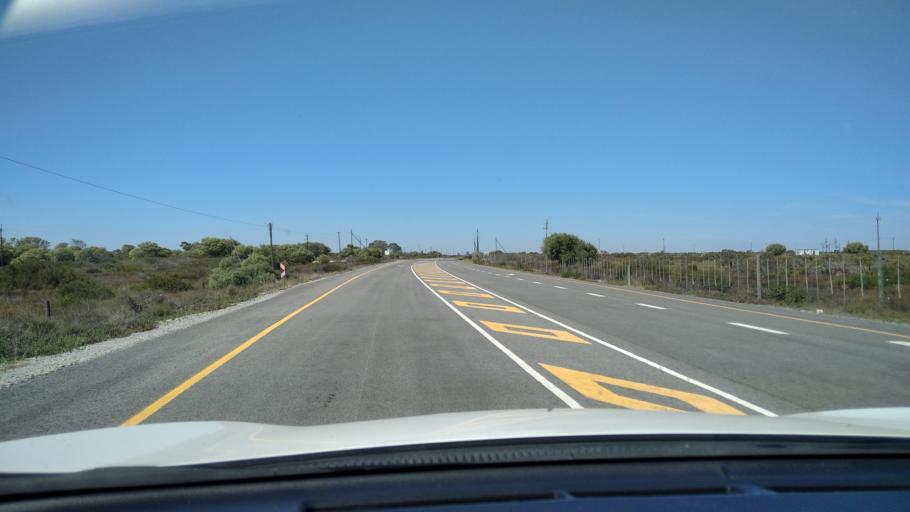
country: ZA
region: Western Cape
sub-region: West Coast District Municipality
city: Vredenburg
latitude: -33.0198
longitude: 18.2628
